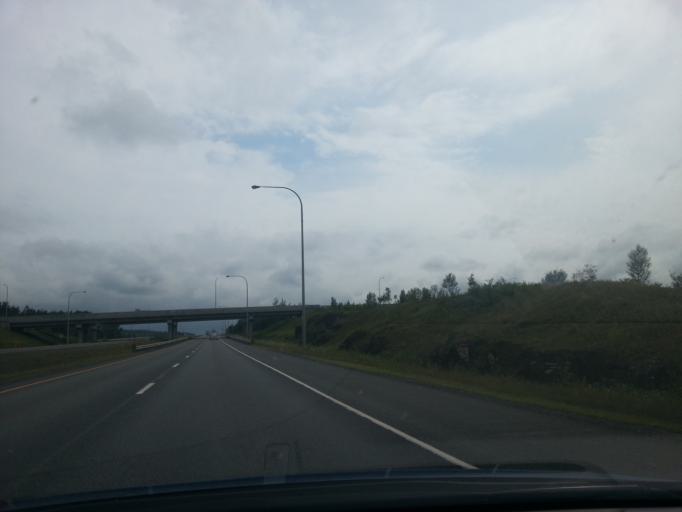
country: US
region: Maine
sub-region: Aroostook County
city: Houlton
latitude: 46.1570
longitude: -67.6090
